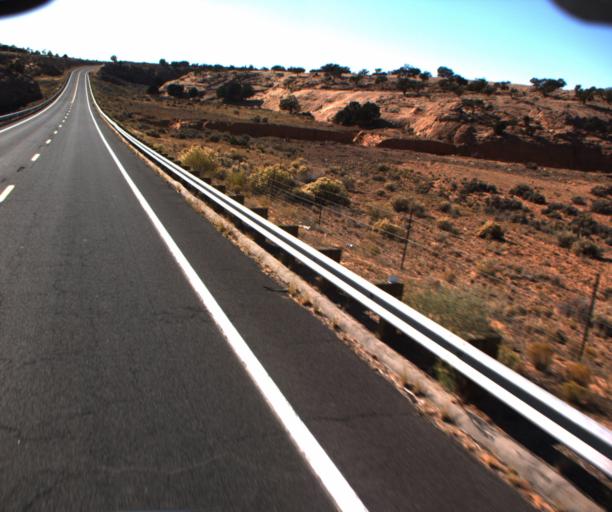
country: US
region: Arizona
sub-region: Coconino County
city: Kaibito
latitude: 36.5620
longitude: -110.7418
